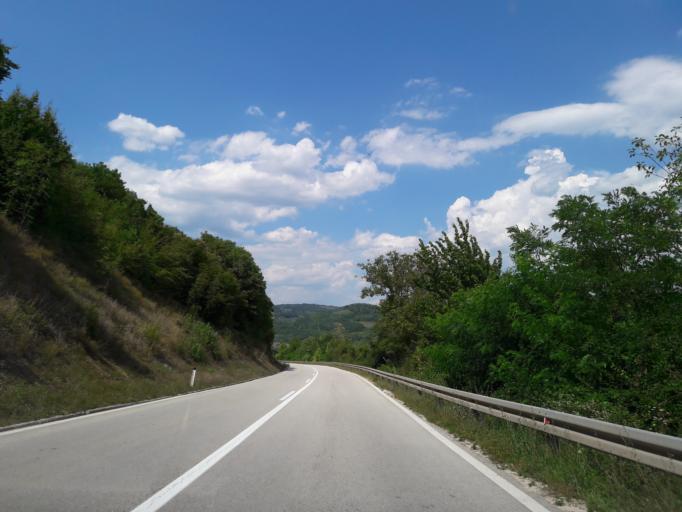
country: BA
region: Republika Srpska
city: Mrkonjic Grad
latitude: 44.5230
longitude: 17.1509
